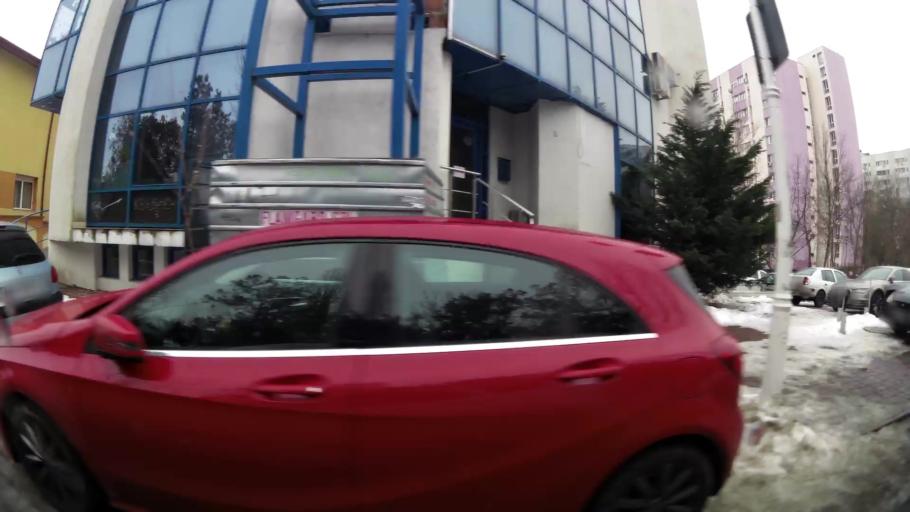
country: RO
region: Ilfov
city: Dobroesti
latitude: 44.4194
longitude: 26.1682
